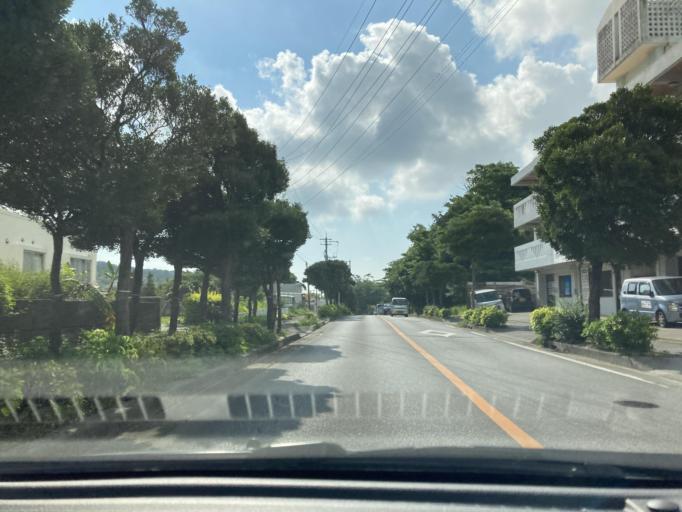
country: JP
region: Okinawa
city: Tomigusuku
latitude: 26.1440
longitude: 127.7656
